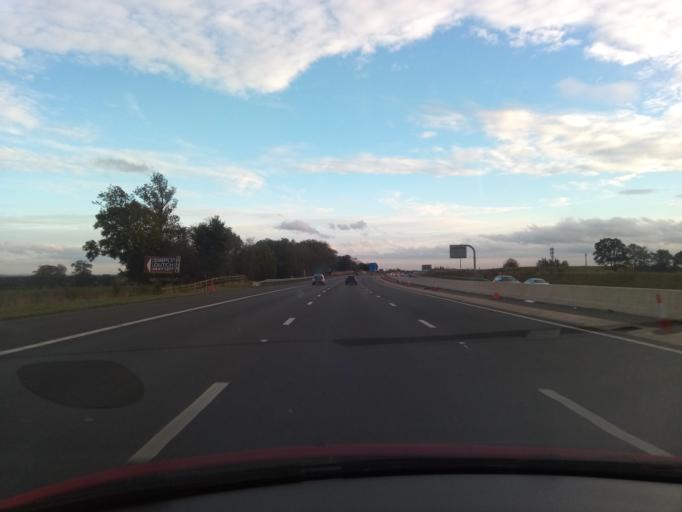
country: GB
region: England
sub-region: North Yorkshire
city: Bedale
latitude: 54.3196
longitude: -1.5748
